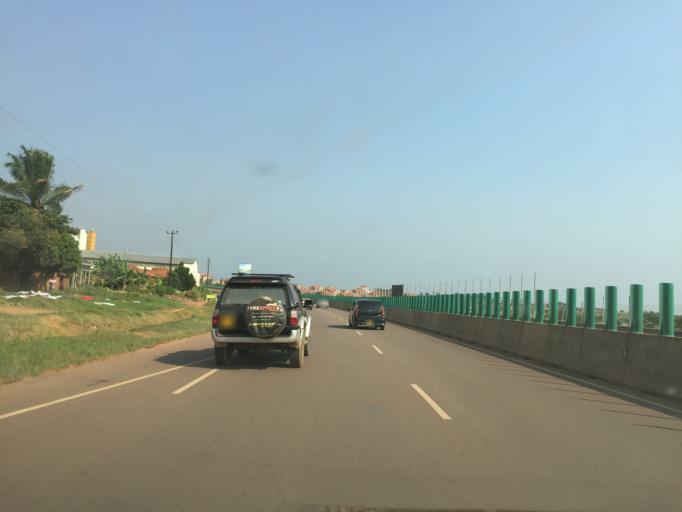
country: UG
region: Central Region
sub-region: Wakiso District
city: Kajansi
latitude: 0.2070
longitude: 32.5901
